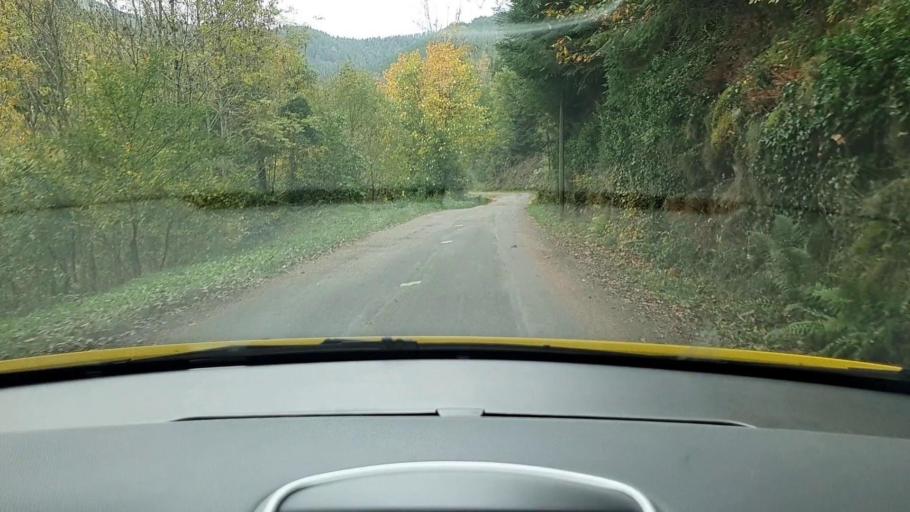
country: FR
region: Languedoc-Roussillon
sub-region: Departement de la Lozere
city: Meyrueis
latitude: 44.1154
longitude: 3.4166
